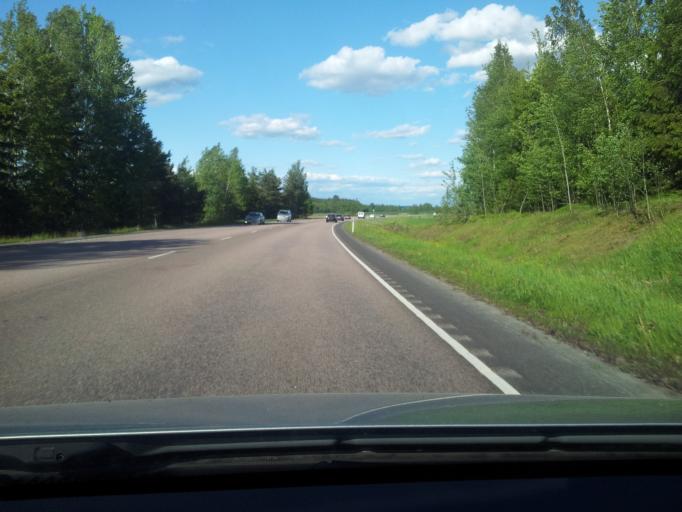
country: FI
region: Kymenlaakso
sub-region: Kouvola
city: Elimaeki
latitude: 60.7230
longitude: 26.3959
